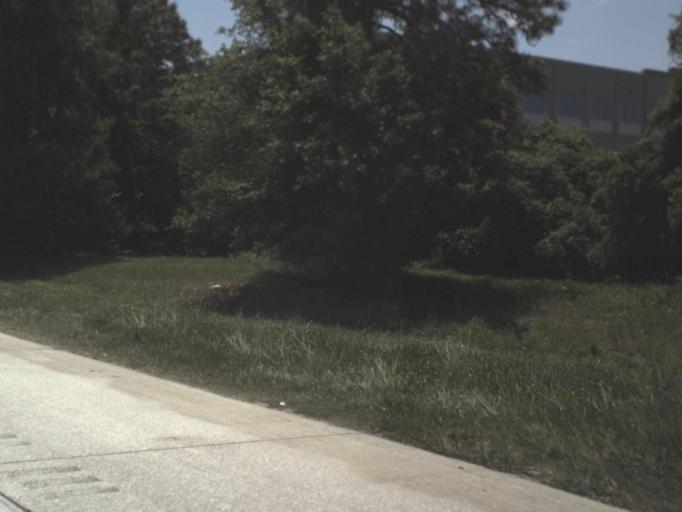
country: US
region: Florida
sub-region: Duval County
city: Jacksonville
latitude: 30.2427
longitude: -81.5876
